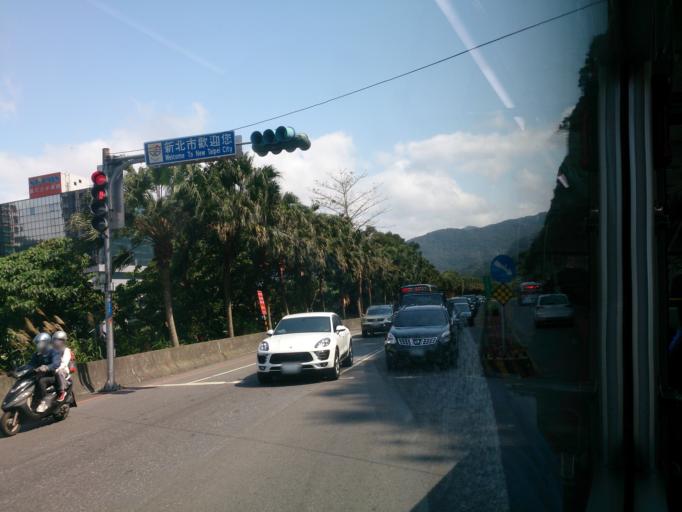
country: TW
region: Taipei
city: Taipei
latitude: 25.0021
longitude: 121.6002
